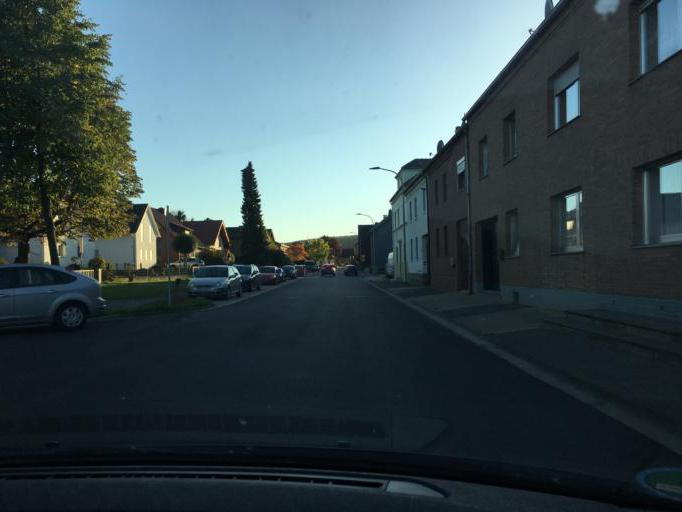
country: DE
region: North Rhine-Westphalia
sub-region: Regierungsbezirk Koln
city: Langerwehe
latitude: 50.8022
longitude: 6.3947
